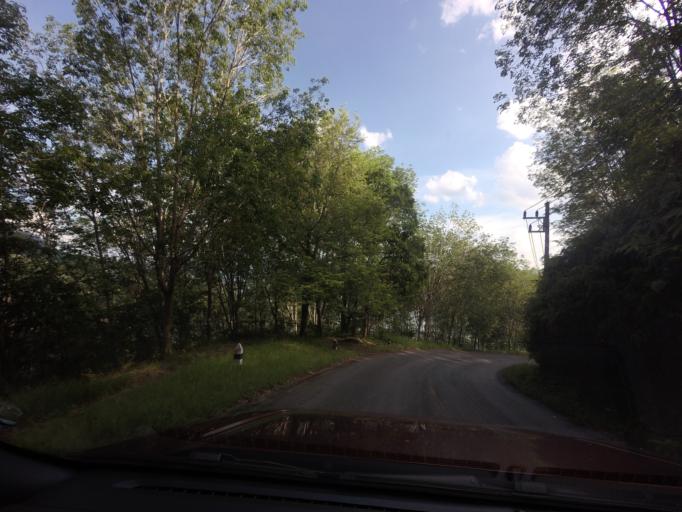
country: TH
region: Yala
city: Than To
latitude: 6.1364
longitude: 101.2927
